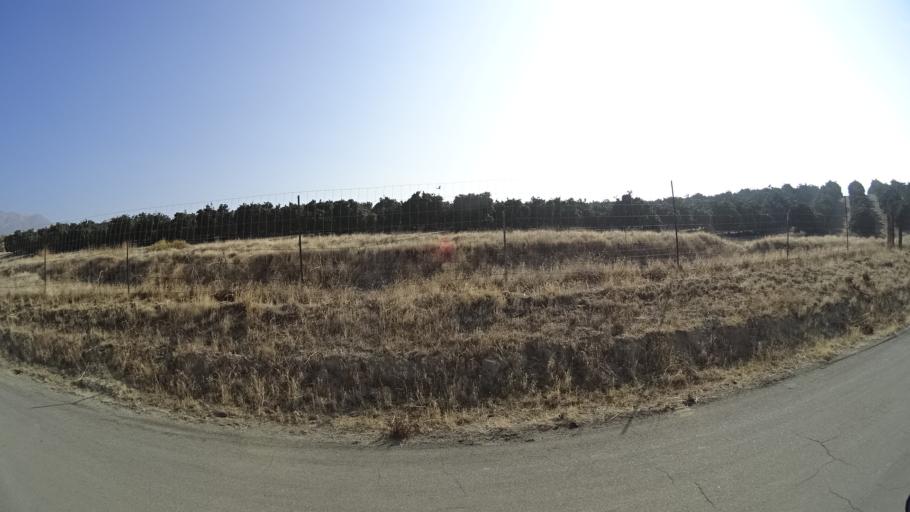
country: US
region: California
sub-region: Kern County
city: Oildale
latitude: 35.4395
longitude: -118.8250
